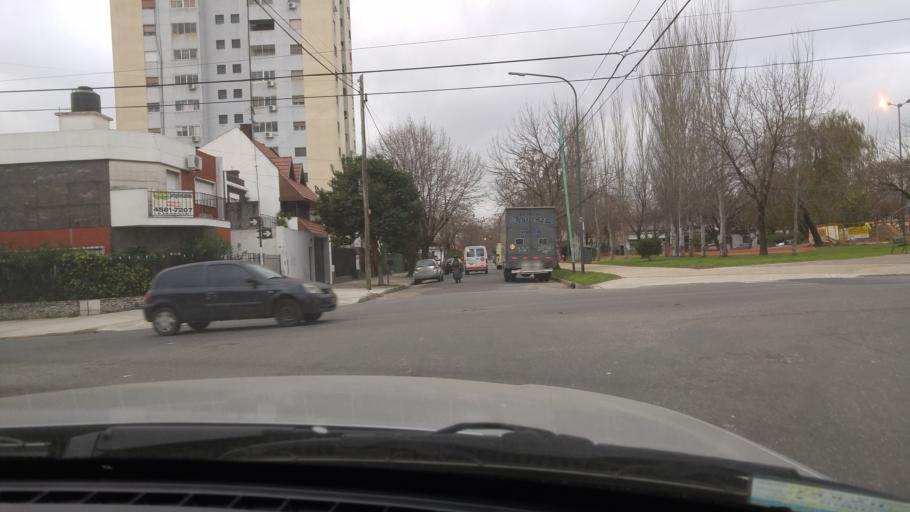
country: AR
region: Buenos Aires
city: Caseros
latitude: -34.6205
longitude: -58.5288
